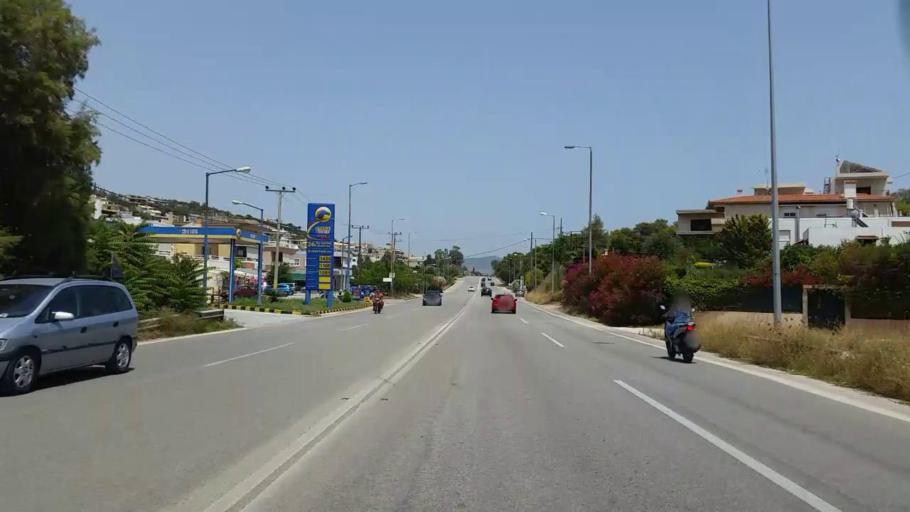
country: GR
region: Attica
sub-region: Nomarchia Anatolikis Attikis
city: Saronida
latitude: 37.7199
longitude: 23.9169
